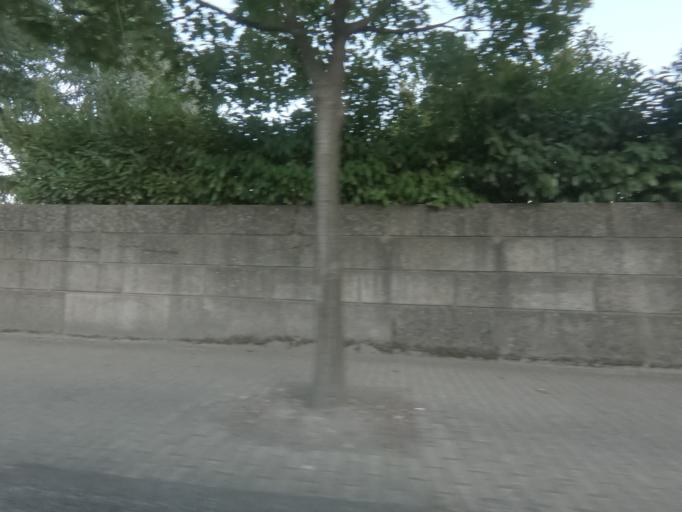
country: PT
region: Vila Real
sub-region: Vila Real
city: Vila Real
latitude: 41.3079
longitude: -7.7401
